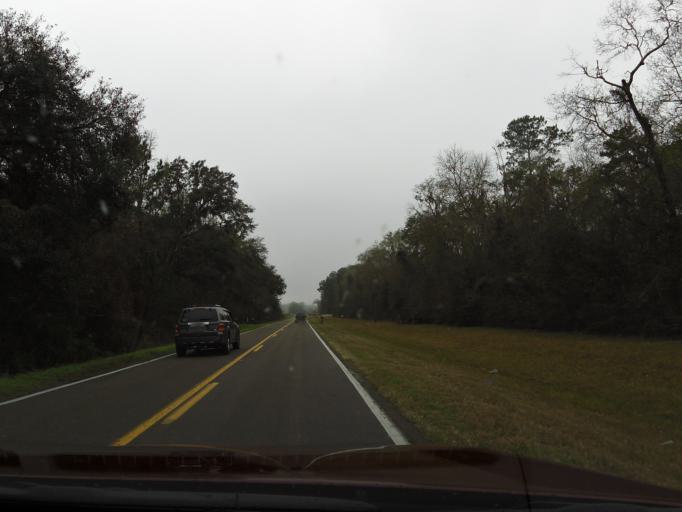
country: US
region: Florida
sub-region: Union County
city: Lake Butler
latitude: 29.9045
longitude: -82.4321
